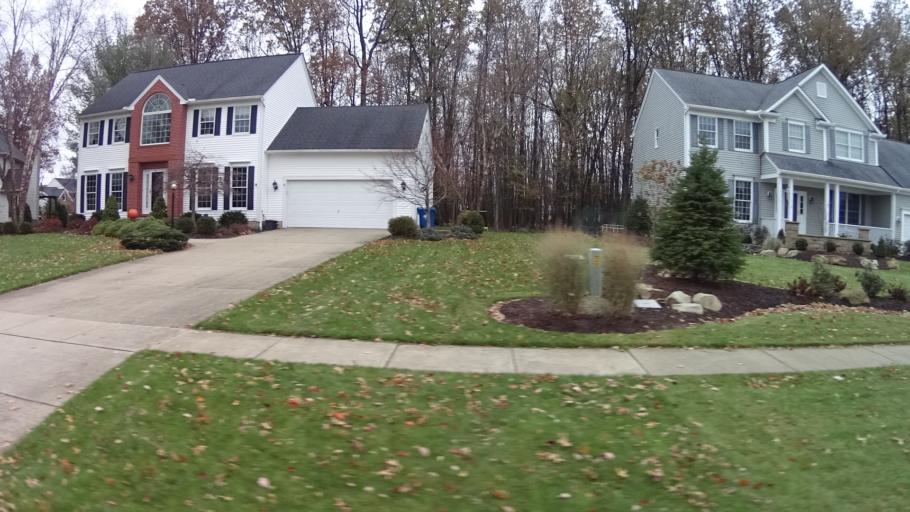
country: US
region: Ohio
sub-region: Lorain County
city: Avon Center
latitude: 41.4850
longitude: -81.9908
